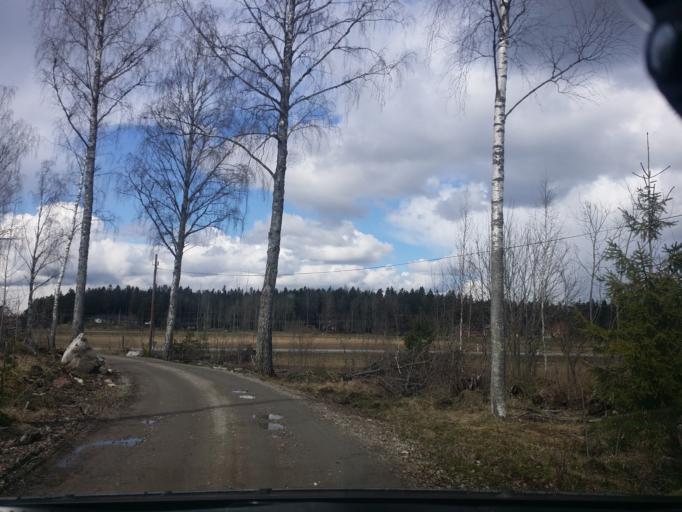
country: SE
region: Vaestmanland
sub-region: Sala Kommun
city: Sala
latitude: 59.9188
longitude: 16.6483
